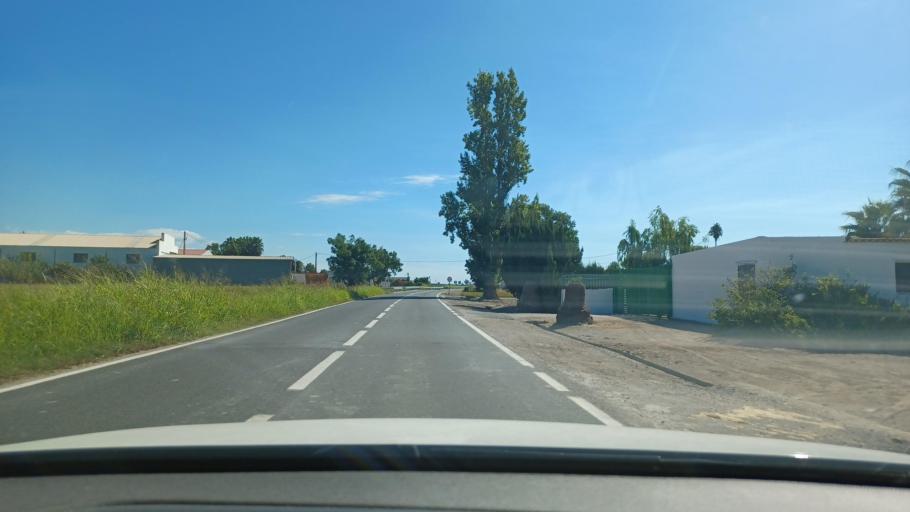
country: ES
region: Catalonia
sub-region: Provincia de Tarragona
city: Amposta
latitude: 40.7046
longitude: 0.6224
